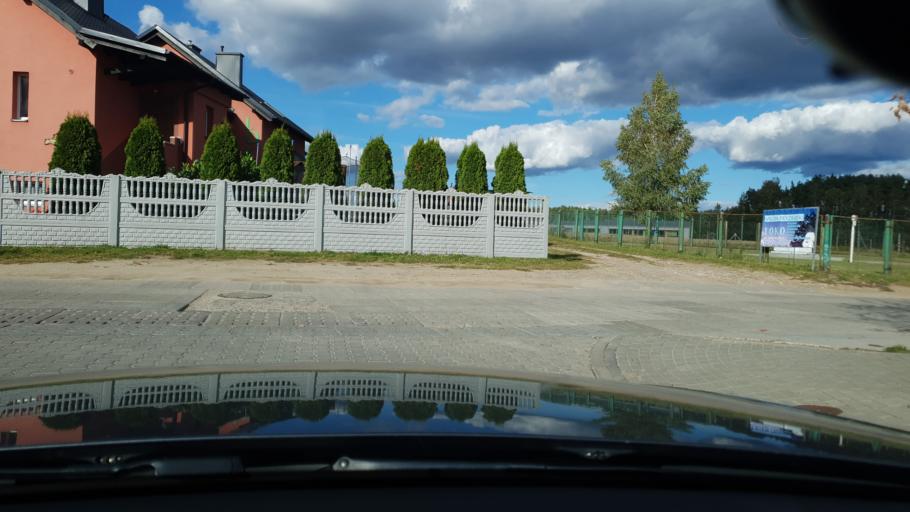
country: PL
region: Pomeranian Voivodeship
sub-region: Powiat kartuski
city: Chwaszczyno
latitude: 54.4943
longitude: 18.4384
